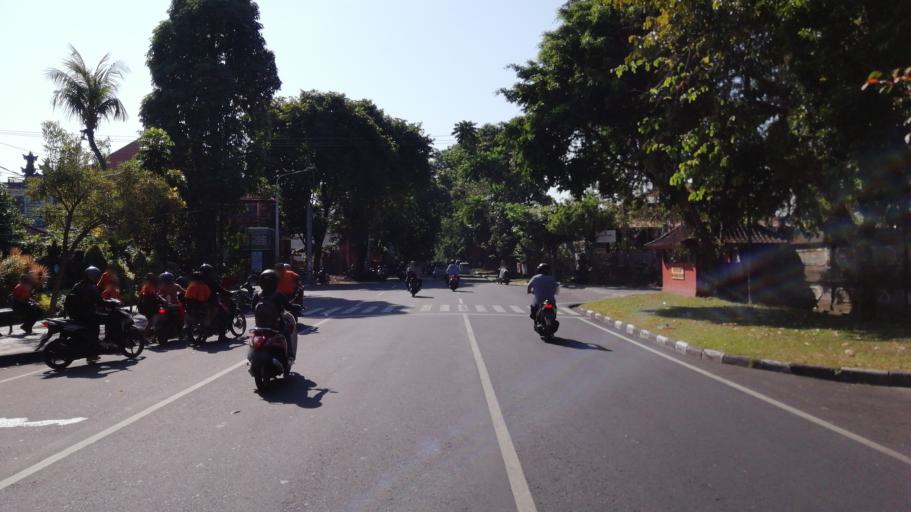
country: ID
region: Bali
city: Denpasar
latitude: -8.6669
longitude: 115.2240
